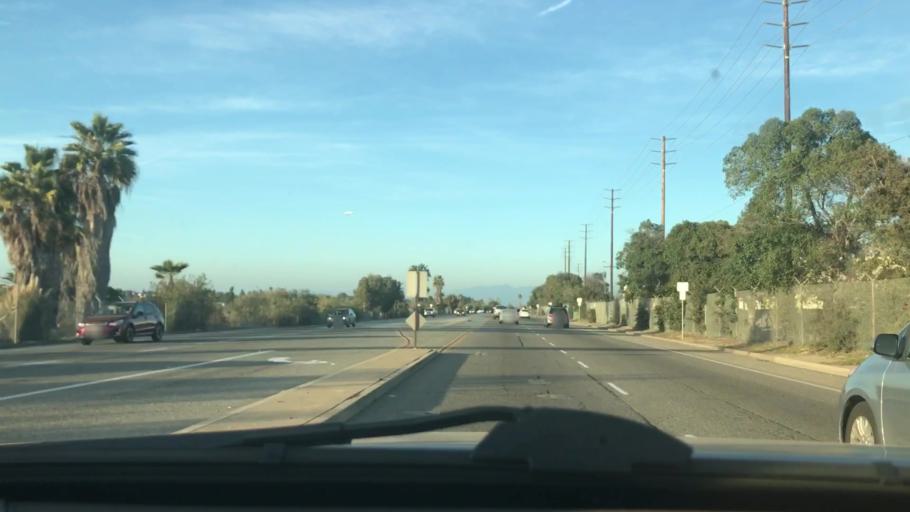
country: US
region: California
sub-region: Orange County
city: Seal Beach
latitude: 33.7611
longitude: -118.1038
